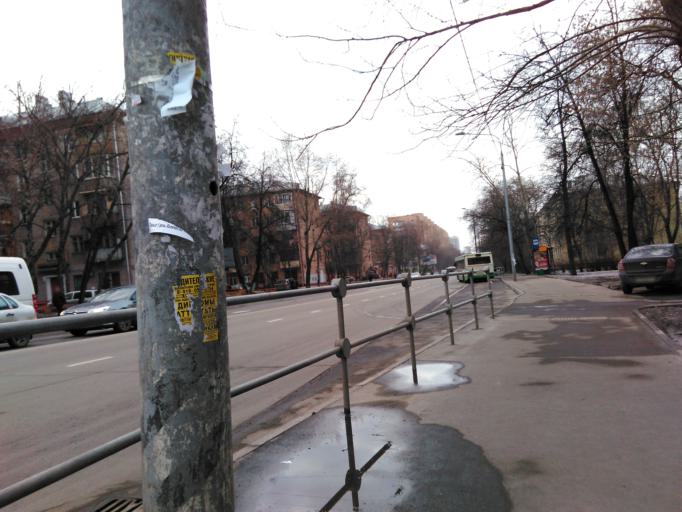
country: RU
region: Moscow
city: Vatutino
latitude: 55.8681
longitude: 37.6751
